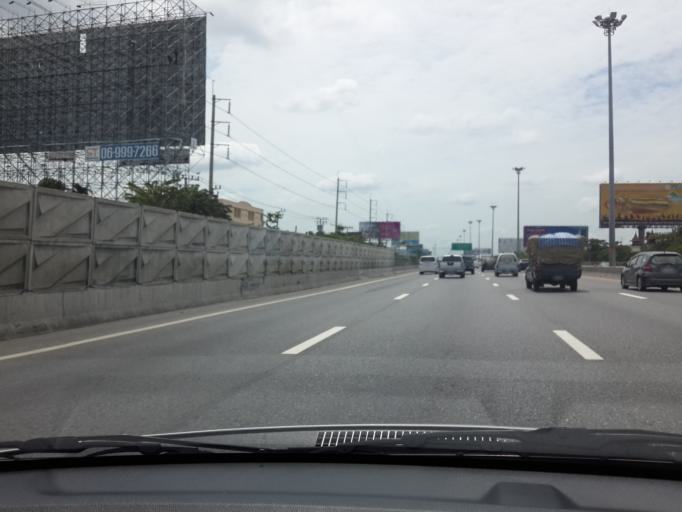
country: TH
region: Bangkok
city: Suan Luang
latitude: 13.7358
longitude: 100.6753
